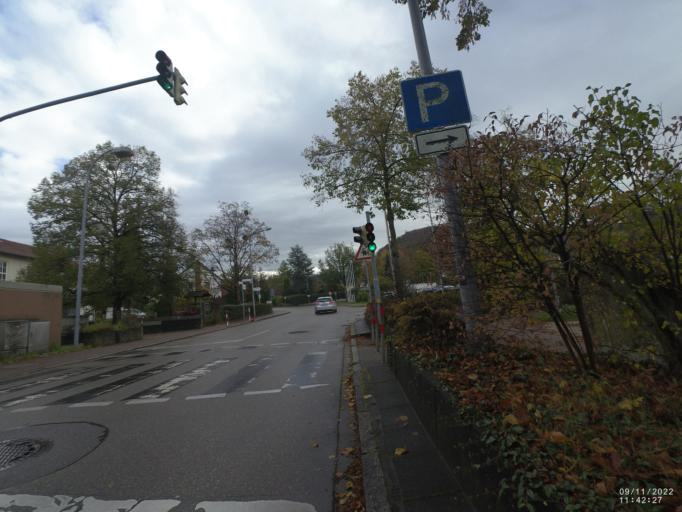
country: DE
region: Baden-Wuerttemberg
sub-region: Regierungsbezirk Stuttgart
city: Geislingen an der Steige
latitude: 48.6252
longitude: 9.8199
